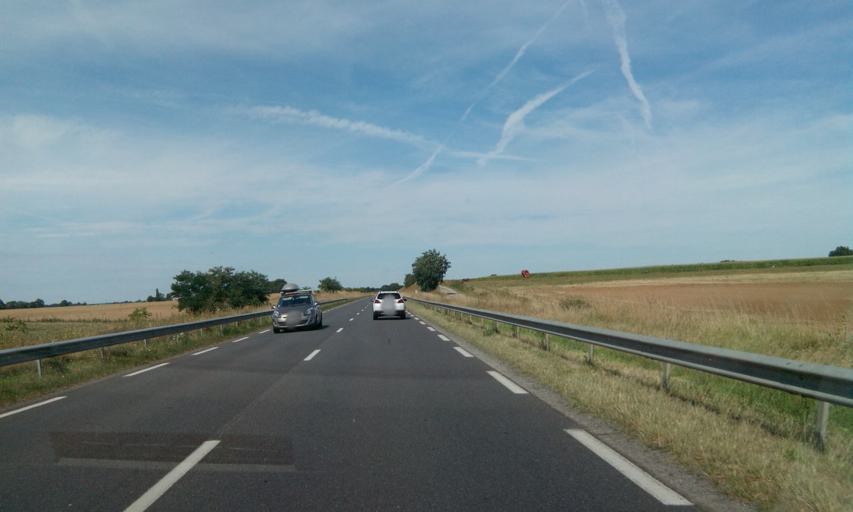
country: FR
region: Poitou-Charentes
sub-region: Departement de la Vienne
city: Charroux
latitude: 46.1537
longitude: 0.3940
